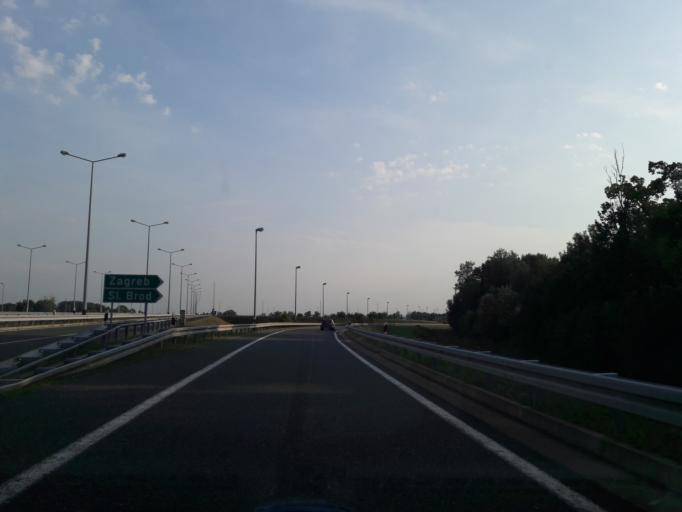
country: HR
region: Brodsko-Posavska
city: Vrpolje
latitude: 45.1494
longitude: 18.3118
